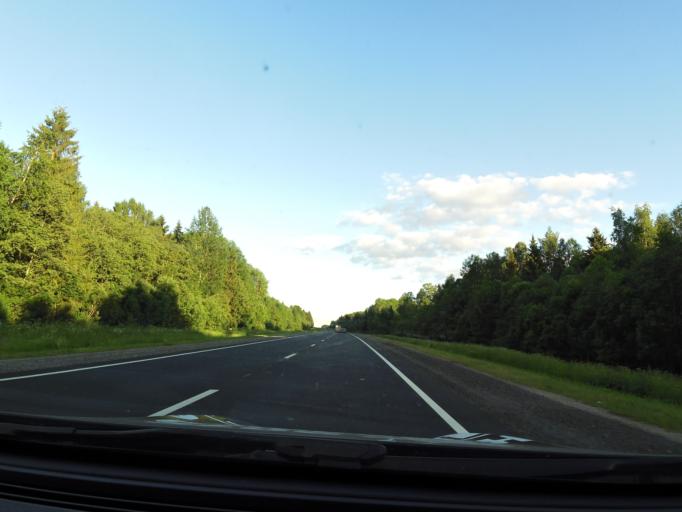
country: RU
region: Vologda
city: Gryazovets
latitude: 59.0067
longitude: 40.1235
